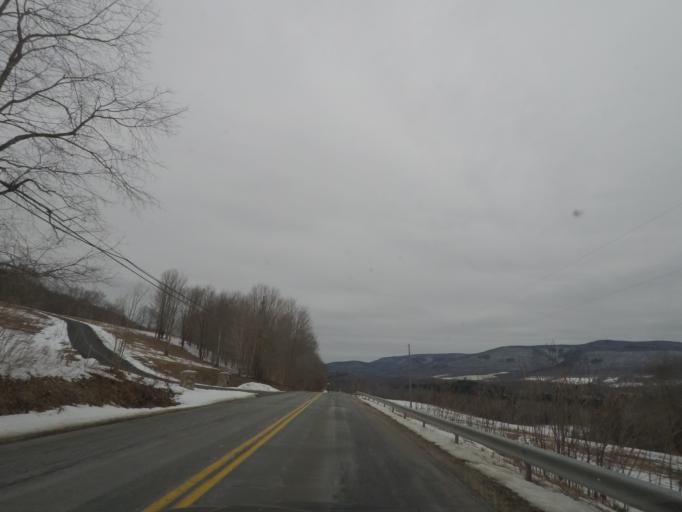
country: US
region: Massachusetts
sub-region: Berkshire County
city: Lanesborough
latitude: 42.5693
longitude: -73.3798
